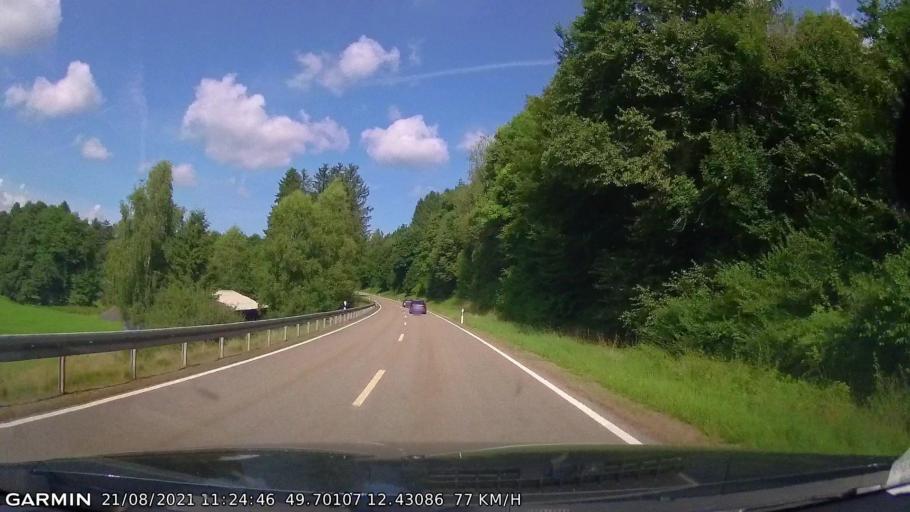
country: DE
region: Bavaria
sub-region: Upper Palatinate
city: Georgenberg
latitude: 49.7011
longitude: 12.4308
